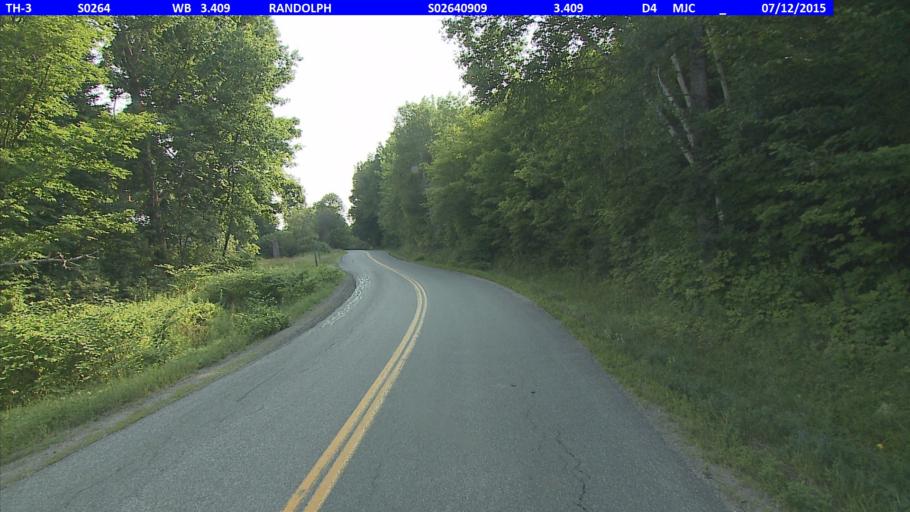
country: US
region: Vermont
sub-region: Orange County
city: Chelsea
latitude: 43.9650
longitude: -72.5136
